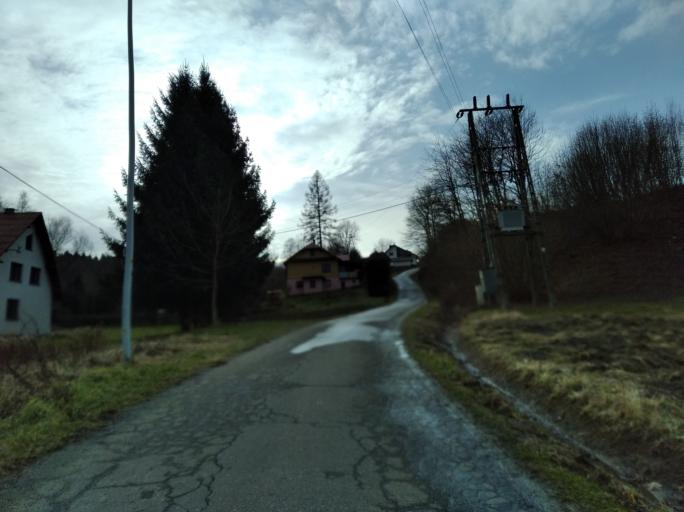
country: PL
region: Subcarpathian Voivodeship
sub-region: Powiat strzyzowski
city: Strzyzow
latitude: 49.8601
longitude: 21.7818
